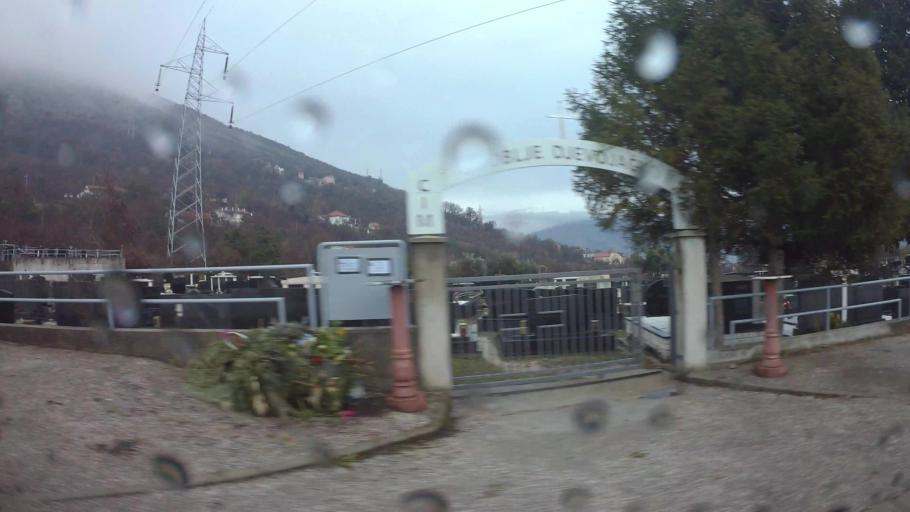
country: BA
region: Federation of Bosnia and Herzegovina
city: Cim
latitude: 43.3558
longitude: 17.7740
